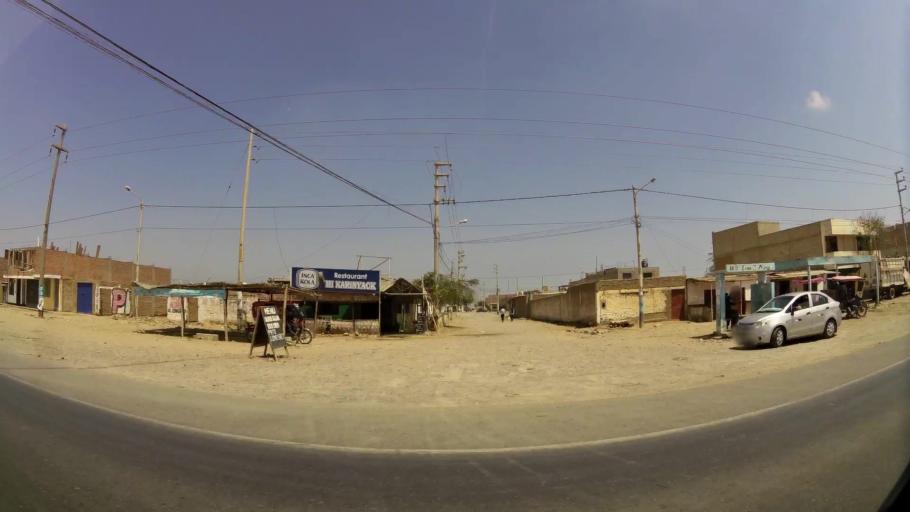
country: PE
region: La Libertad
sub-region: Provincia de Pacasmayo
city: Pacasmayo
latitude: -7.4176
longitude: -79.5463
